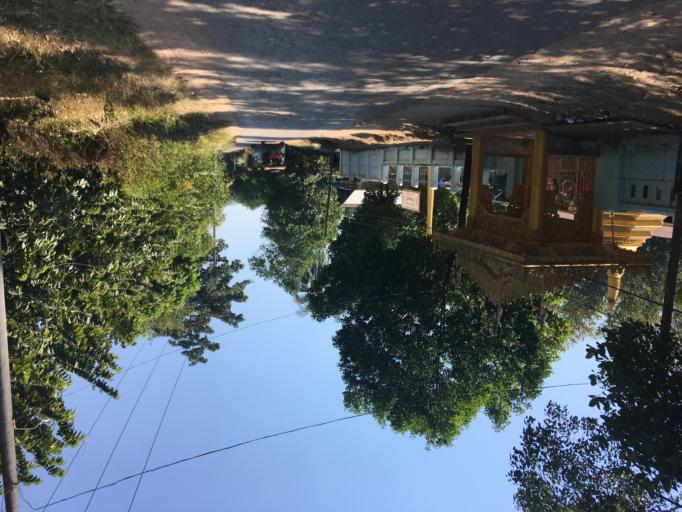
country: MM
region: Mon
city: Mawlamyine
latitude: 16.4341
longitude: 97.6995
